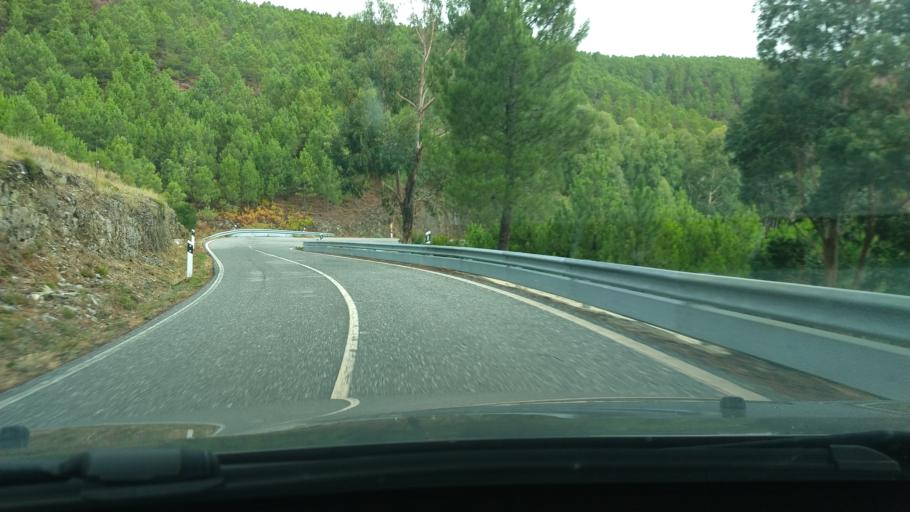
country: PT
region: Castelo Branco
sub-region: Covilha
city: Covilha
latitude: 40.2345
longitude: -7.6673
